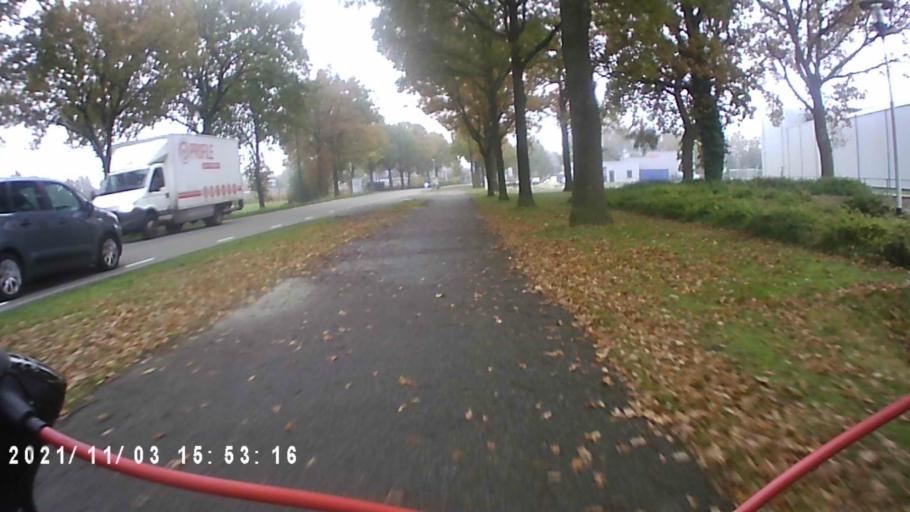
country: NL
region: Groningen
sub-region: Gemeente Leek
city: Leek
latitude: 53.0719
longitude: 6.3319
